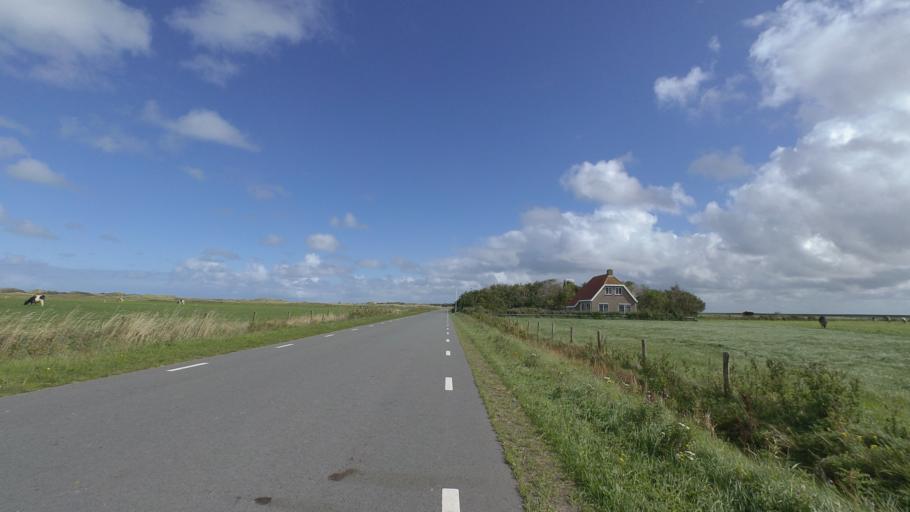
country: NL
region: Friesland
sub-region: Gemeente Ameland
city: Nes
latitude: 53.4500
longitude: 5.8255
